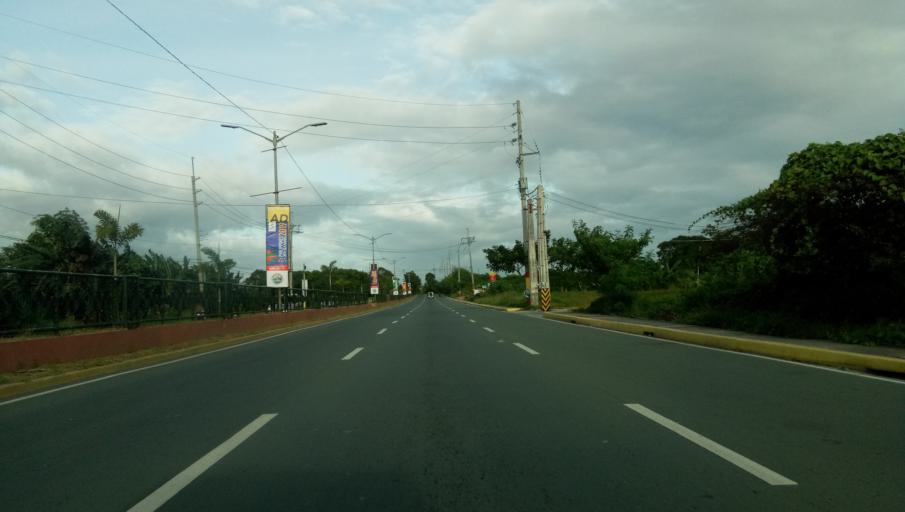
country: PH
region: Calabarzon
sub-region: Province of Cavite
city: Dasmarinas
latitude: 14.3766
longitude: 120.9496
